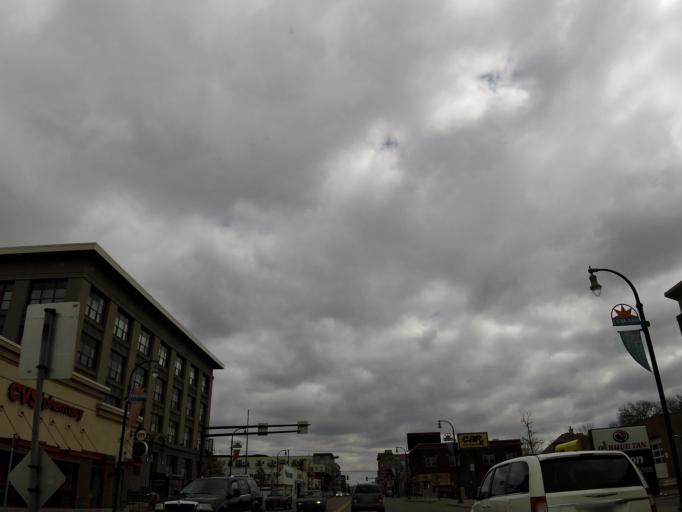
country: US
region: Minnesota
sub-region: Hennepin County
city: Minneapolis
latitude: 44.9484
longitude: -93.2930
